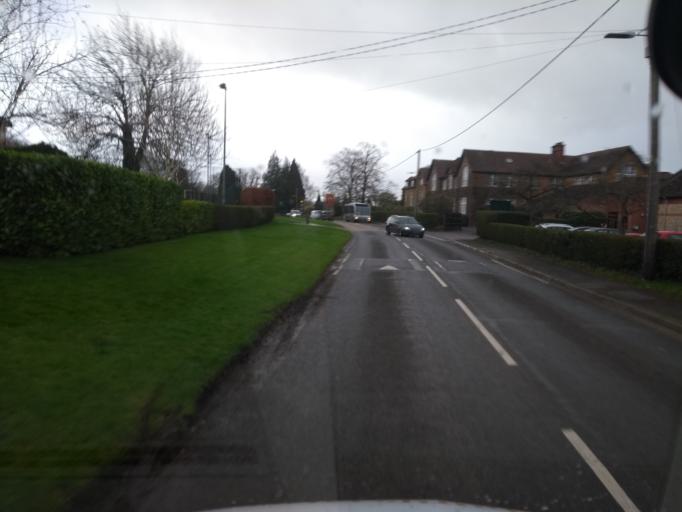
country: GB
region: England
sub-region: Somerset
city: Bruton
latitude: 51.1002
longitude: -2.4671
